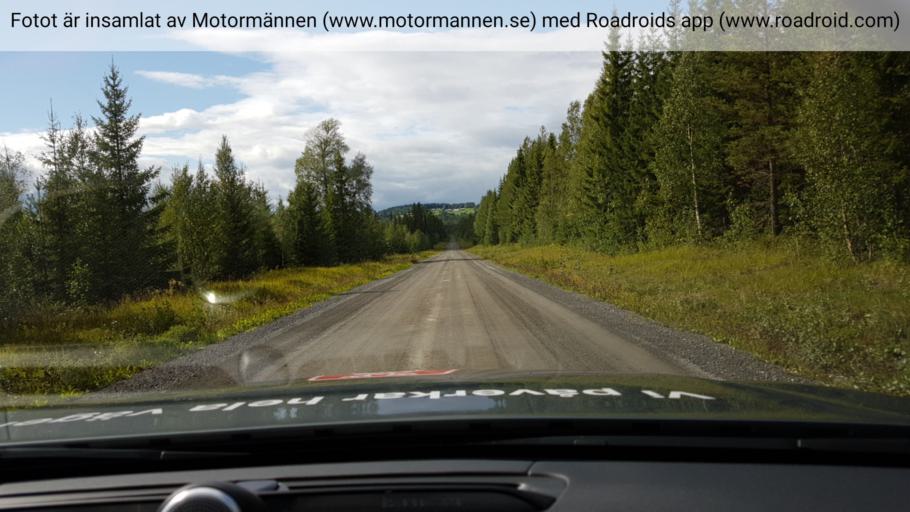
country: SE
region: Jaemtland
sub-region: OEstersunds Kommun
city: Lit
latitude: 63.6791
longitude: 14.7847
